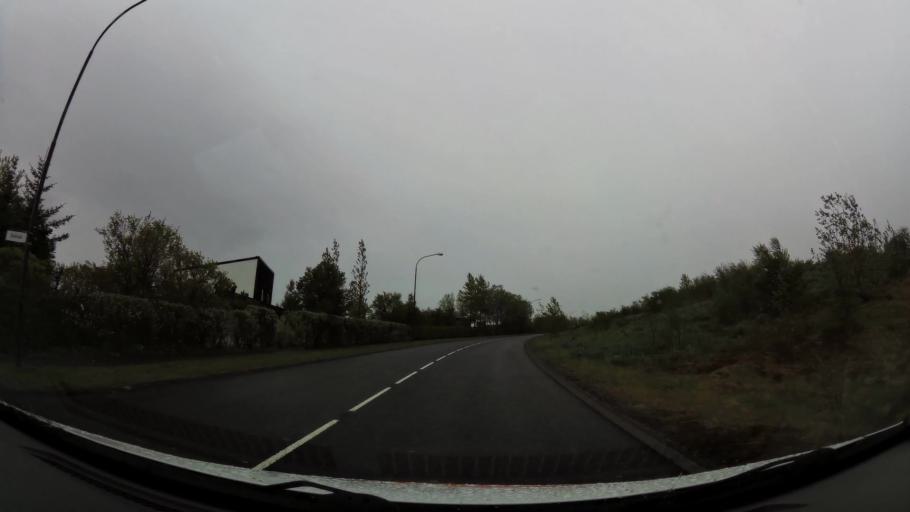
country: IS
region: Capital Region
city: Kopavogur
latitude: 64.0904
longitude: -21.8895
